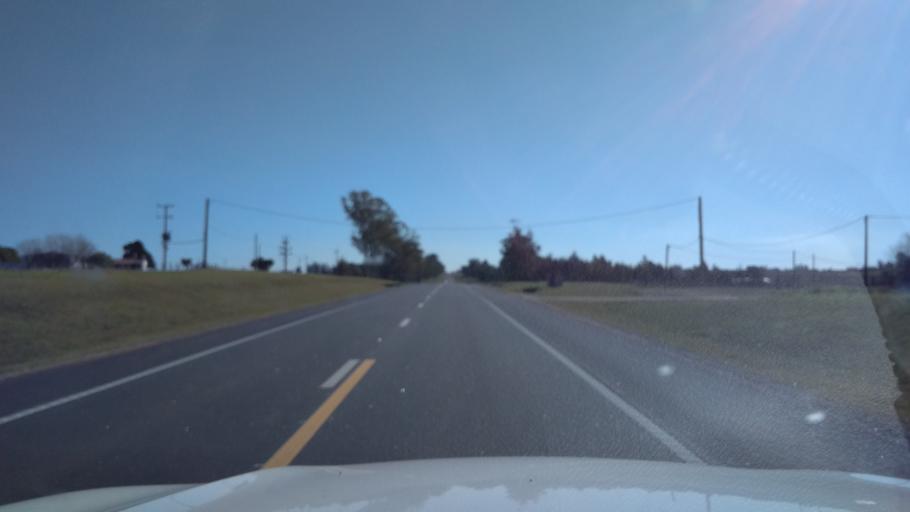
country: UY
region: Canelones
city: Santa Rosa
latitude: -34.5253
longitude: -55.9678
